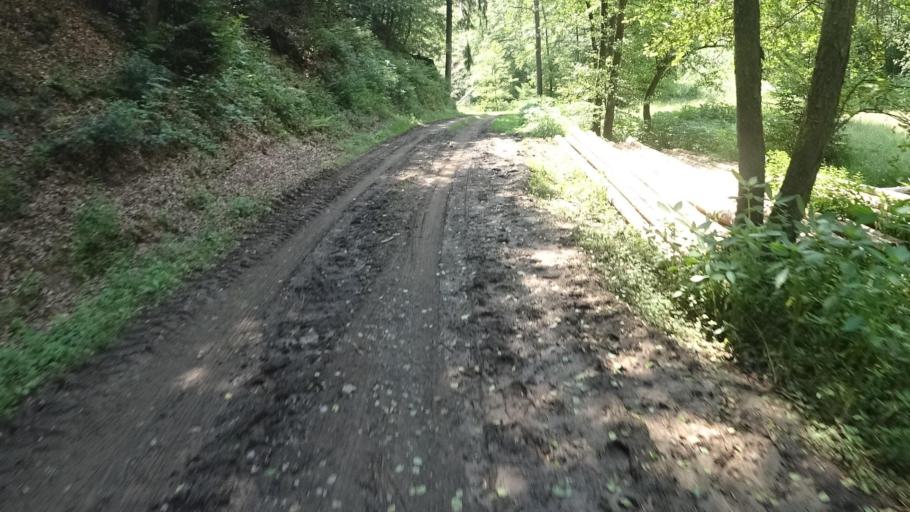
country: DE
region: Rheinland-Pfalz
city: Sankt Katharinen
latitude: 50.5880
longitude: 7.3833
